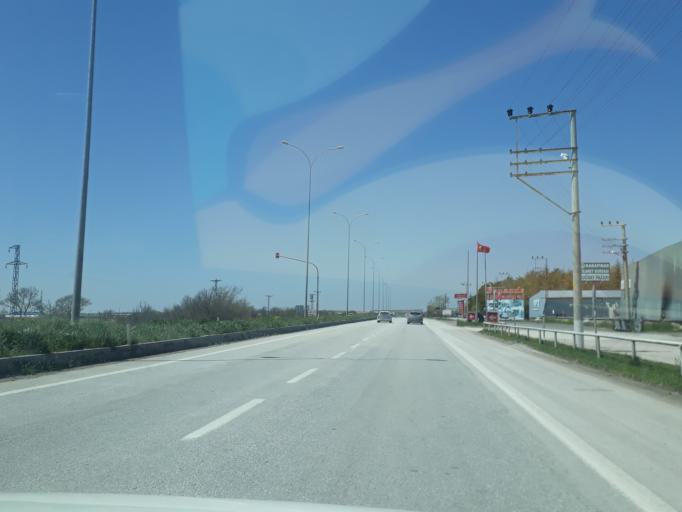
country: TR
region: Konya
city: Karapinar
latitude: 37.7149
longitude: 33.5138
